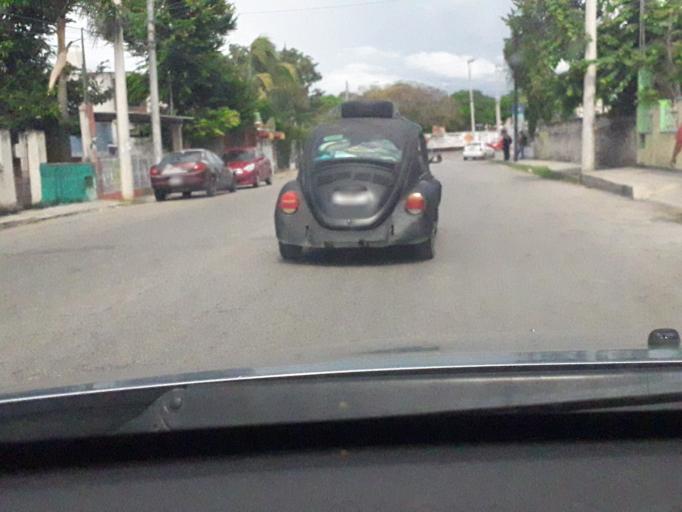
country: MX
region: Yucatan
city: Merida
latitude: 20.9714
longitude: -89.6569
